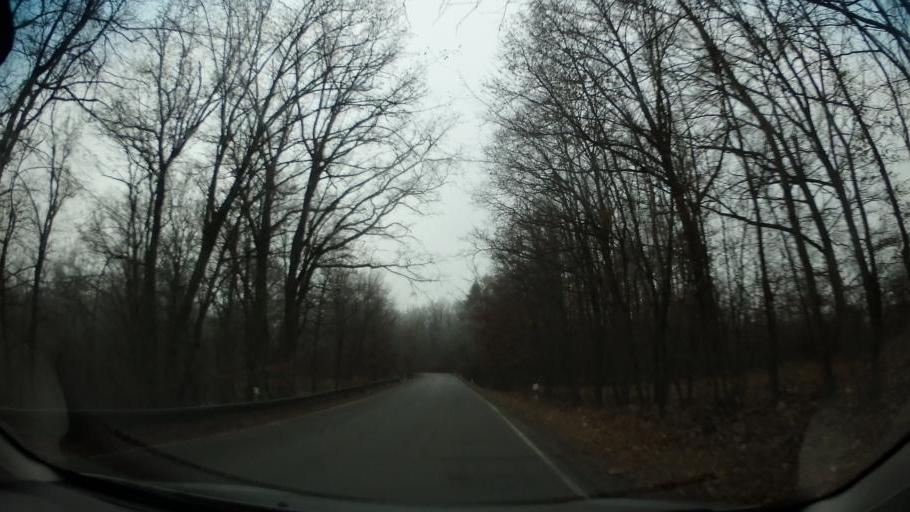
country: CZ
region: Vysocina
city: Mohelno
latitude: 49.1391
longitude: 16.2037
